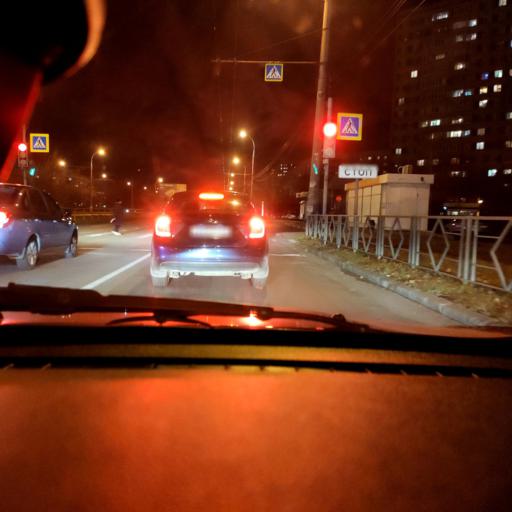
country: RU
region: Samara
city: Tol'yatti
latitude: 53.5232
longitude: 49.3229
